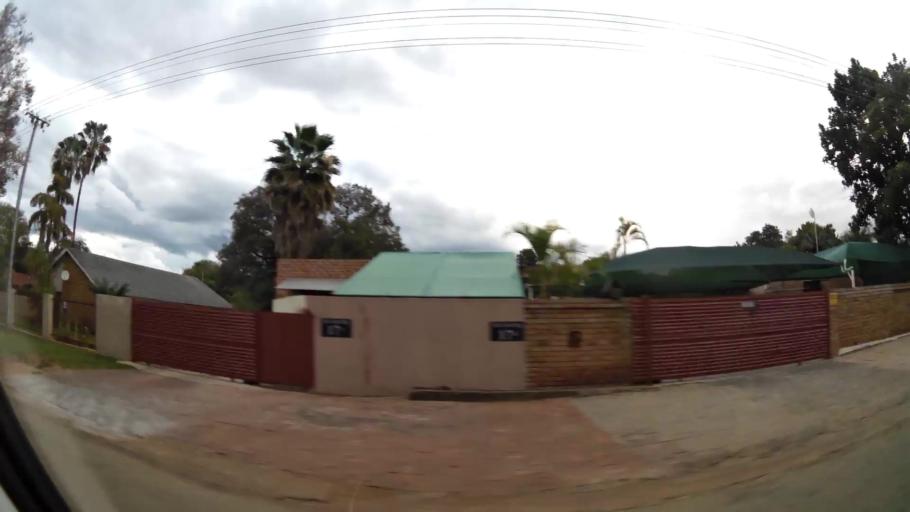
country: ZA
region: Limpopo
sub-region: Waterberg District Municipality
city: Mokopane
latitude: -24.1928
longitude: 28.9950
